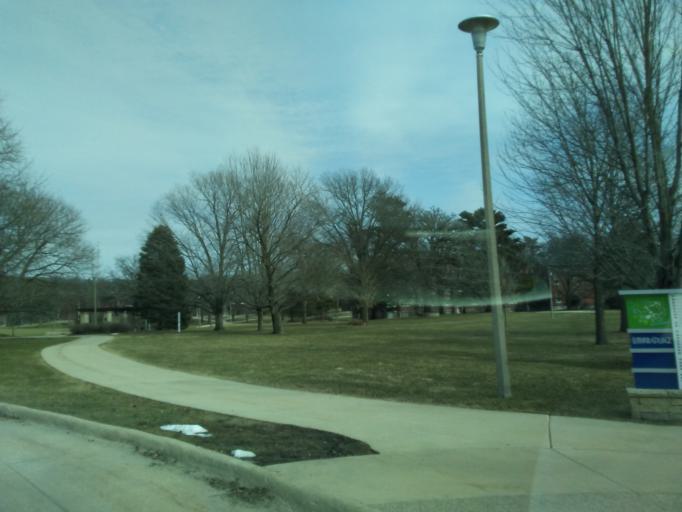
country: US
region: Iowa
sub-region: Winneshiek County
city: Decorah
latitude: 43.3117
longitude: -91.8058
